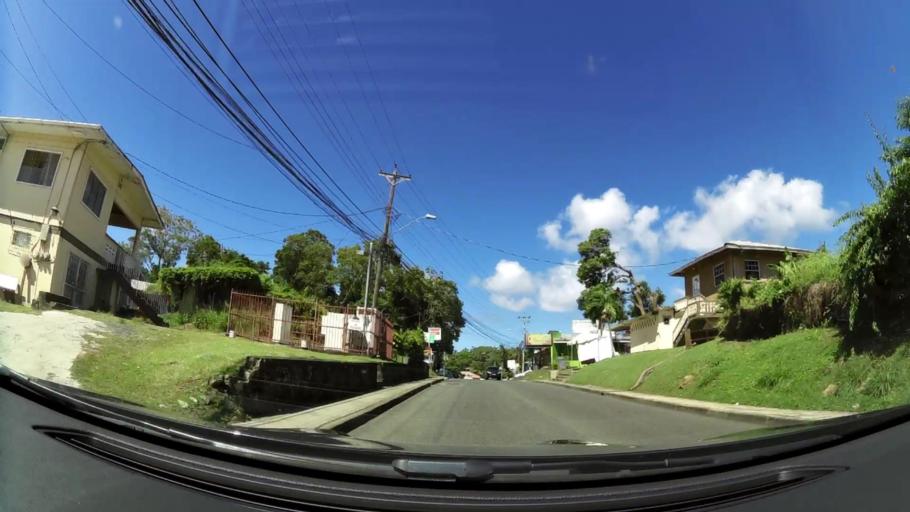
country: TT
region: Tobago
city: Scarborough
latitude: 11.1698
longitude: -60.7822
